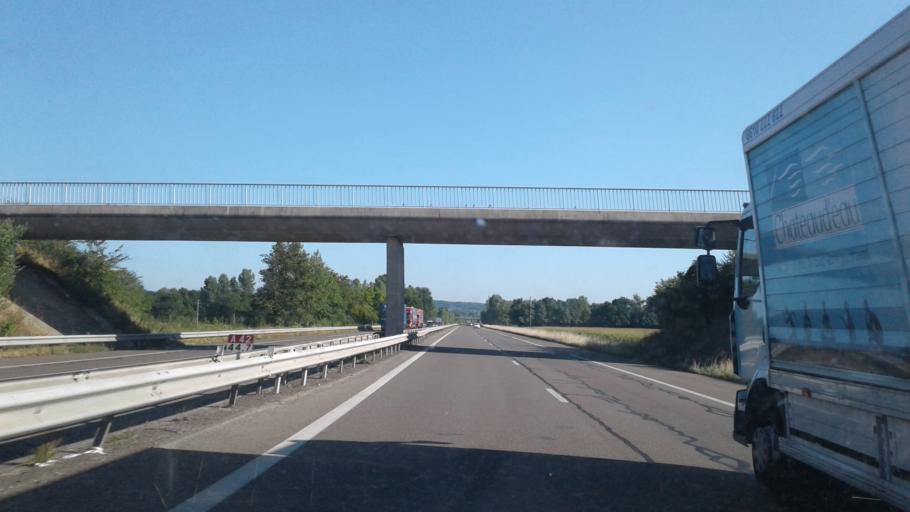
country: FR
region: Rhone-Alpes
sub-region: Departement de l'Ain
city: Priay
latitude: 45.9998
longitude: 5.3129
